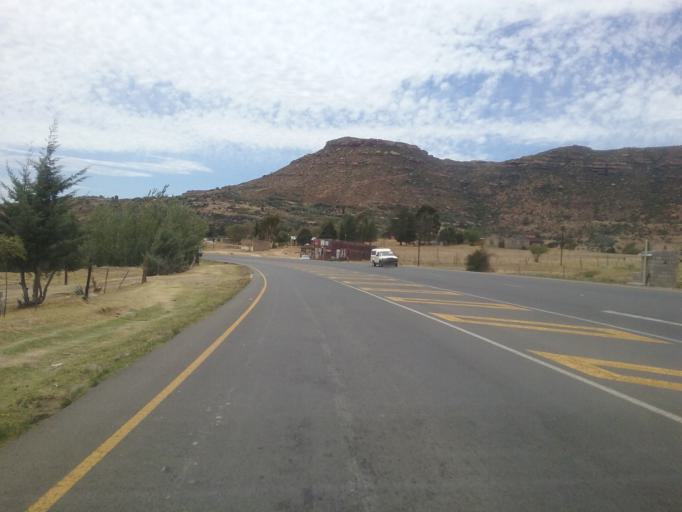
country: LS
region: Maseru
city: Nako
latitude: -29.6449
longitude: 27.4732
